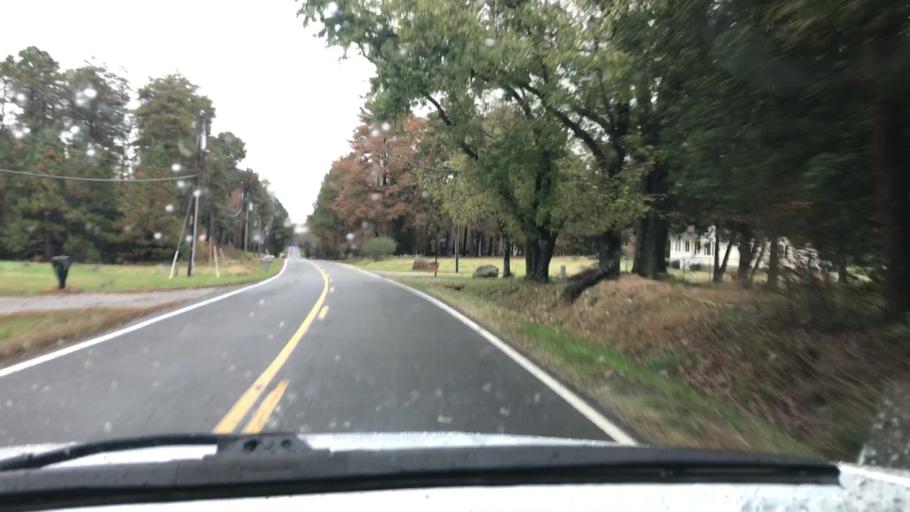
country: US
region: Virginia
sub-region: Henrico County
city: Short Pump
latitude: 37.6232
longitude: -77.6911
